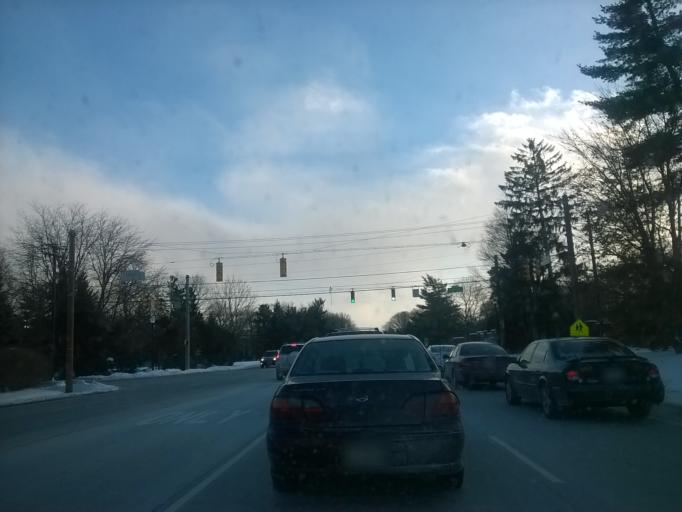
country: US
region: Indiana
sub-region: Marion County
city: Meridian Hills
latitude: 39.8908
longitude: -86.1579
